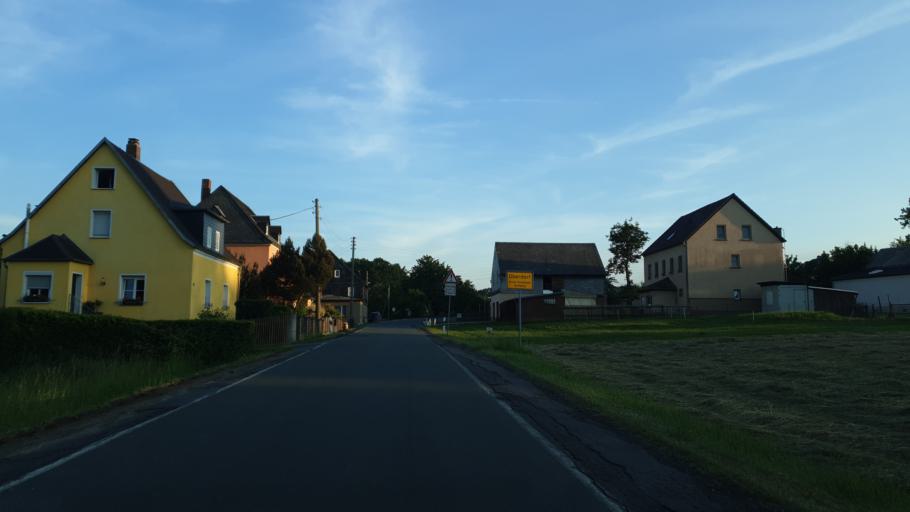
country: DE
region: Saxony
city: Stollberg
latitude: 50.6846
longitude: 12.7427
